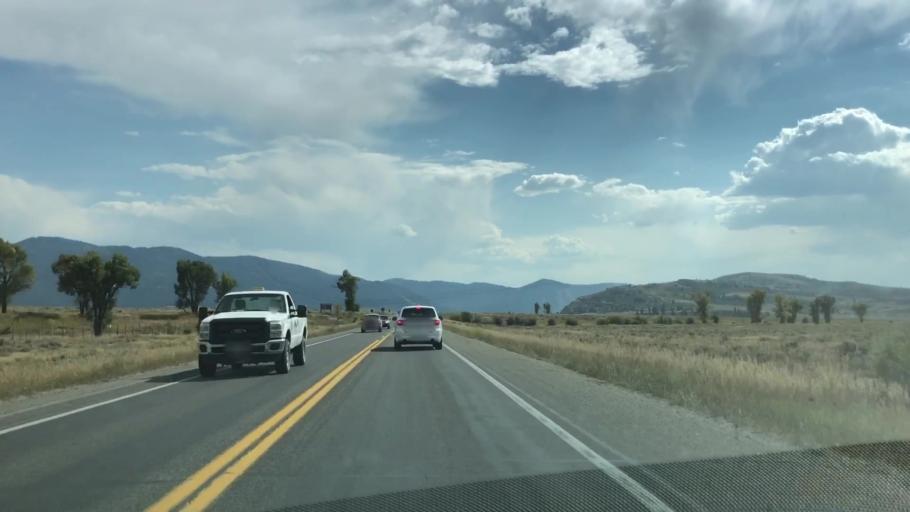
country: US
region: Wyoming
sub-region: Teton County
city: Jackson
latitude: 43.5618
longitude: -110.7330
